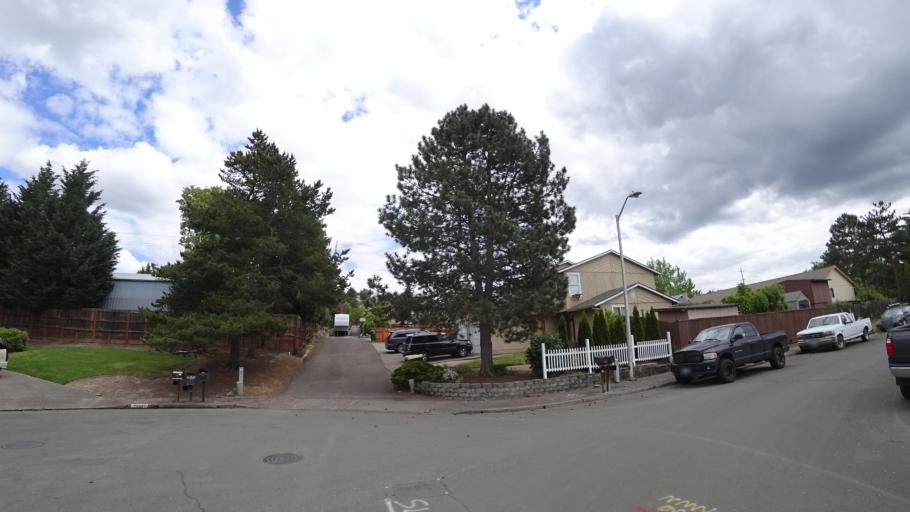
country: US
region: Oregon
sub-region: Washington County
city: Aloha
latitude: 45.4720
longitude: -122.8532
